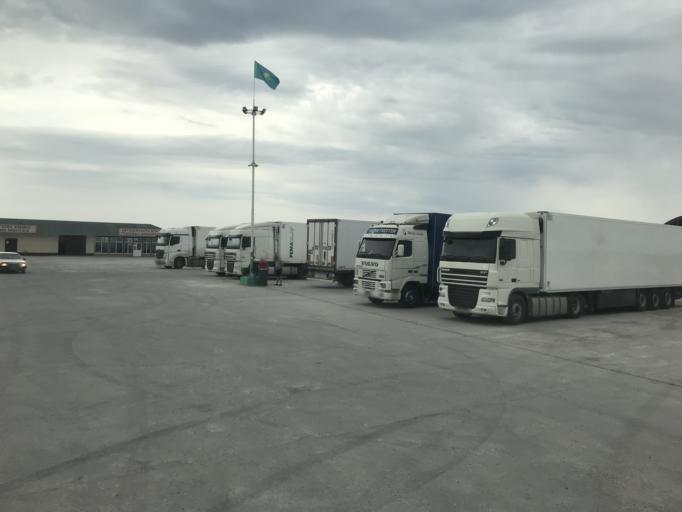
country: KZ
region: Ongtustik Qazaqstan
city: Asykata
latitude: 40.9624
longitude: 68.4611
